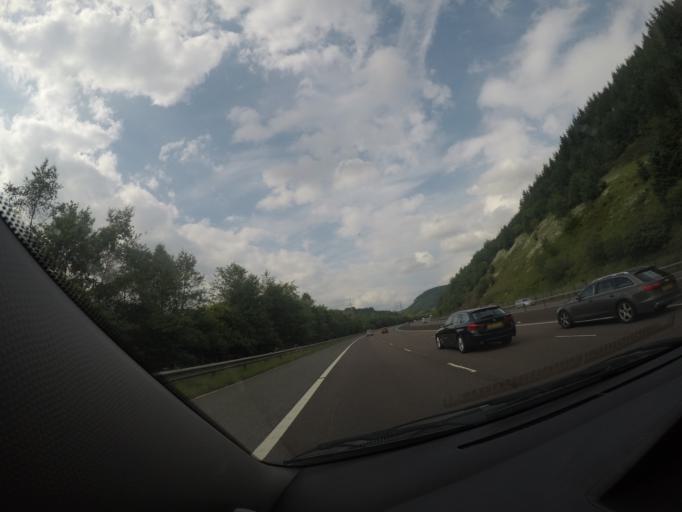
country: GB
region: Scotland
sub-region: Dumfries and Galloway
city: Moffat
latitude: 55.3614
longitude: -3.5156
